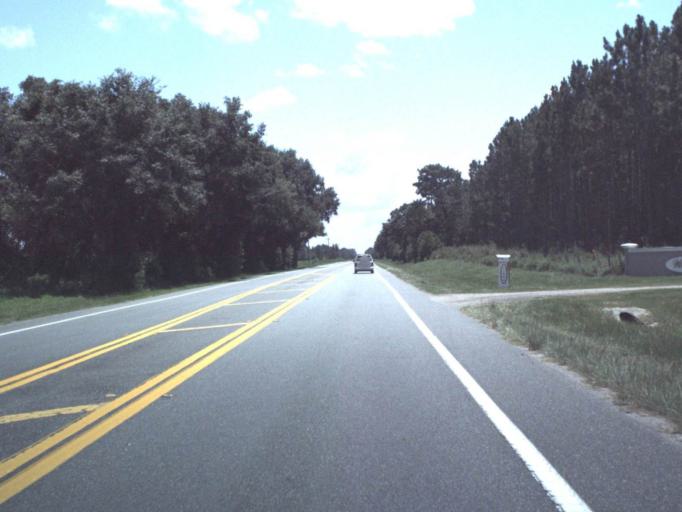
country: US
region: Florida
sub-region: Columbia County
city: Lake City
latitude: 30.0169
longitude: -82.7103
